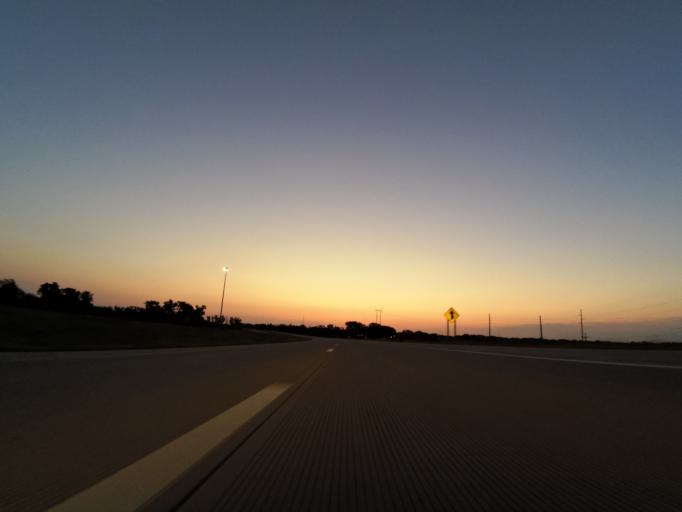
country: US
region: Kansas
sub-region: Reno County
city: South Hutchinson
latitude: 38.0131
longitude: -97.9191
